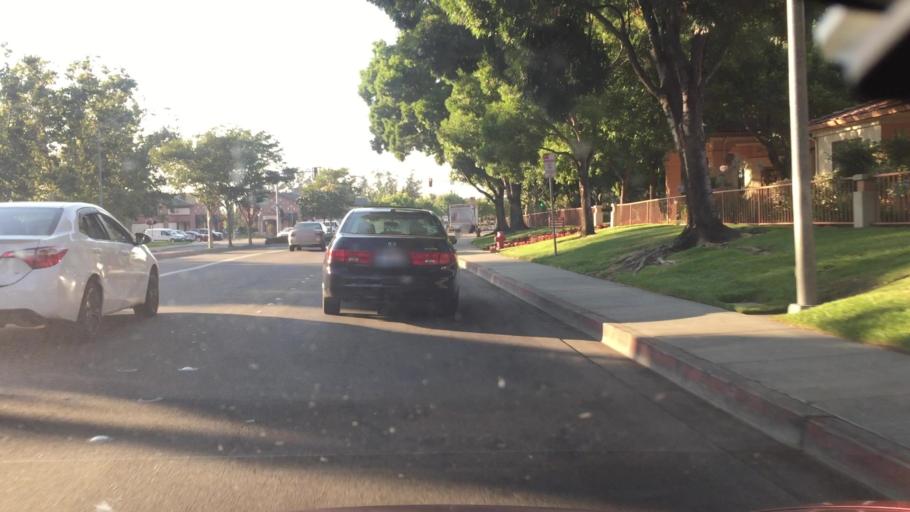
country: US
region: California
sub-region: Alameda County
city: Livermore
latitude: 37.6902
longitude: -121.7726
